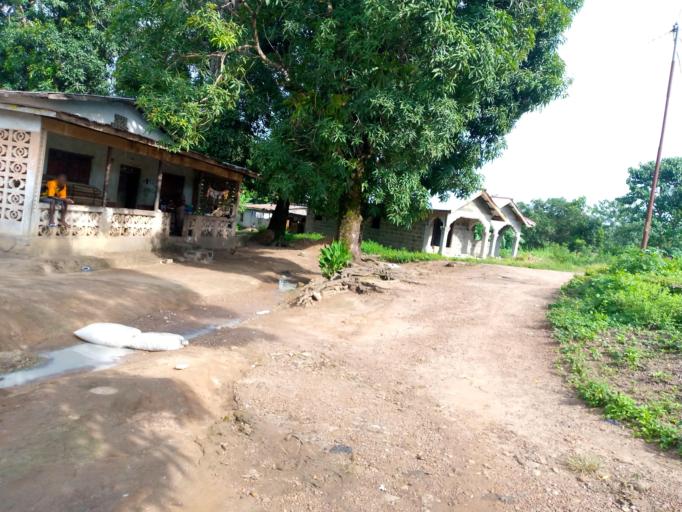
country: SL
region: Northern Province
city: Magburaka
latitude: 8.7198
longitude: -11.9529
